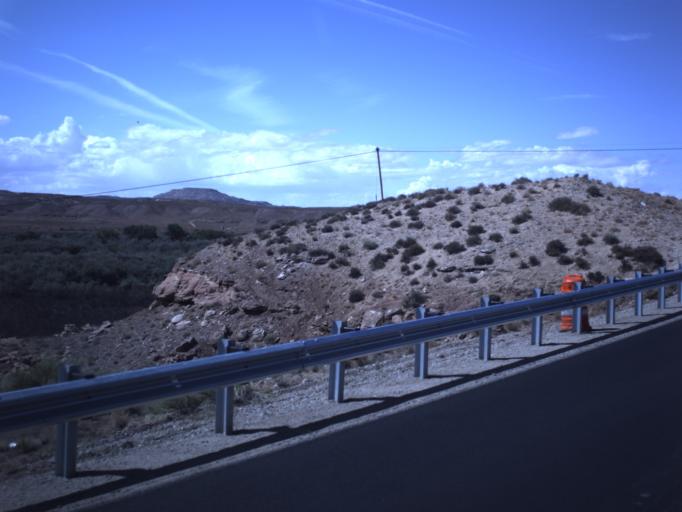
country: US
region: Utah
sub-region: San Juan County
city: Blanding
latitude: 37.2378
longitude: -109.2295
